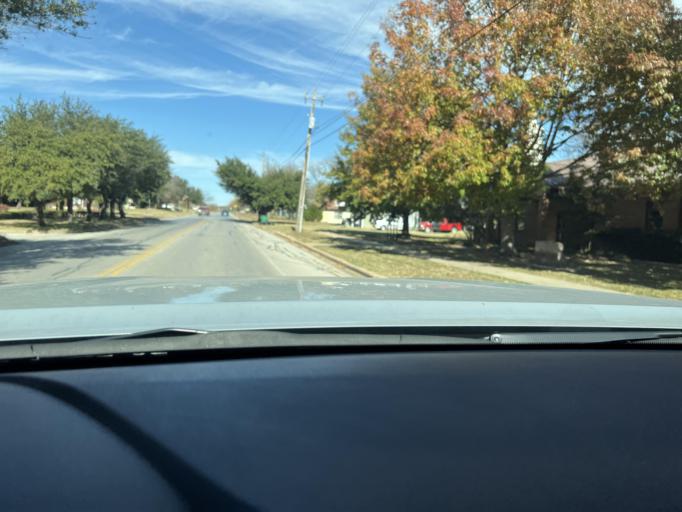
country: US
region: Texas
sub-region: Eastland County
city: Eastland
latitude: 32.3945
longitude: -98.8181
